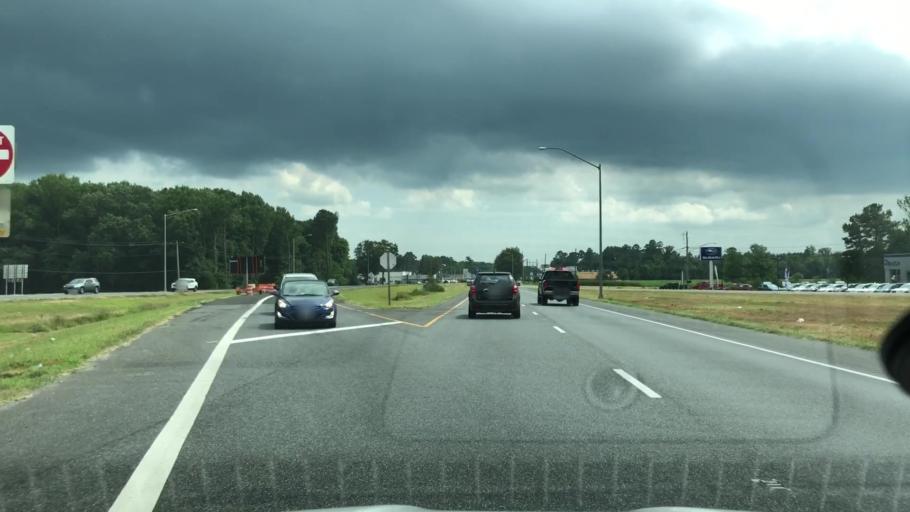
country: US
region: Maryland
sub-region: Worcester County
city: Pocomoke City
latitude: 38.0583
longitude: -75.5447
